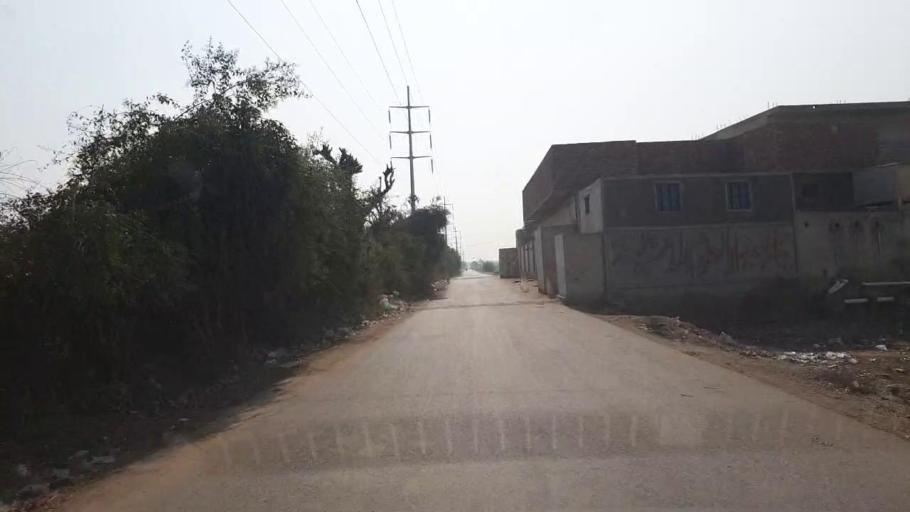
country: PK
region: Sindh
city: Hala
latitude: 25.8334
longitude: 68.4202
